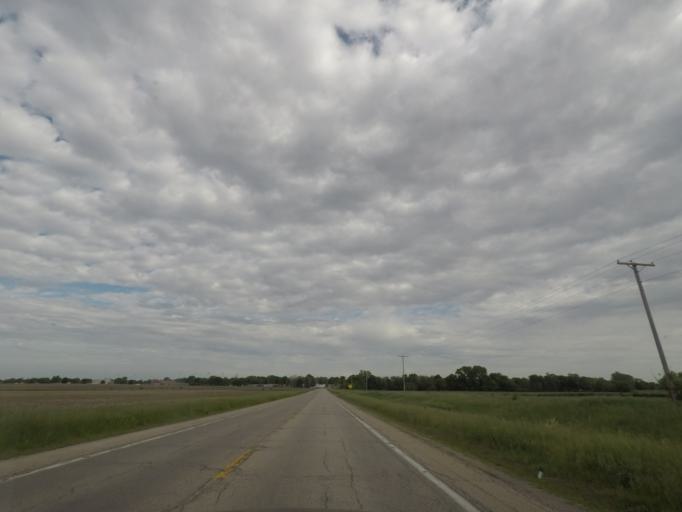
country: US
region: Illinois
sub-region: Logan County
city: Lincoln
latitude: 40.1306
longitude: -89.3444
